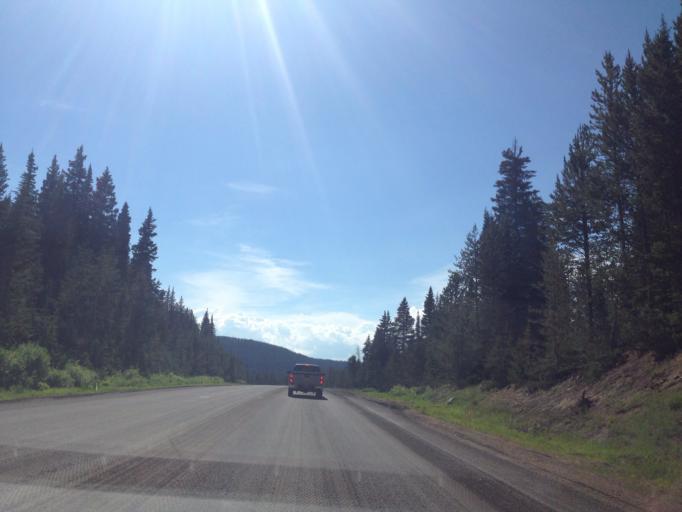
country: US
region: Colorado
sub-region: Routt County
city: Steamboat Springs
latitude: 40.3841
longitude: -106.7030
